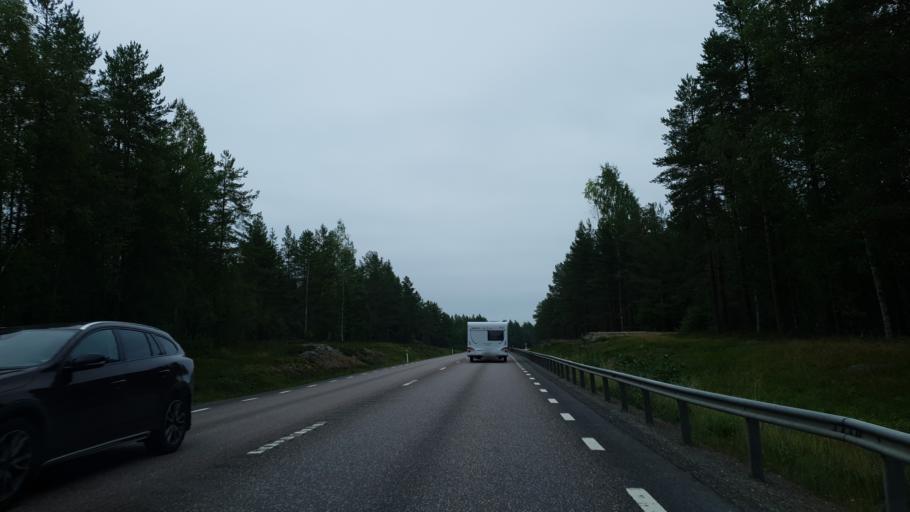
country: SE
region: Vaesterbotten
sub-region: Skelleftea Kommun
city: Burea
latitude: 64.3294
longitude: 21.1990
